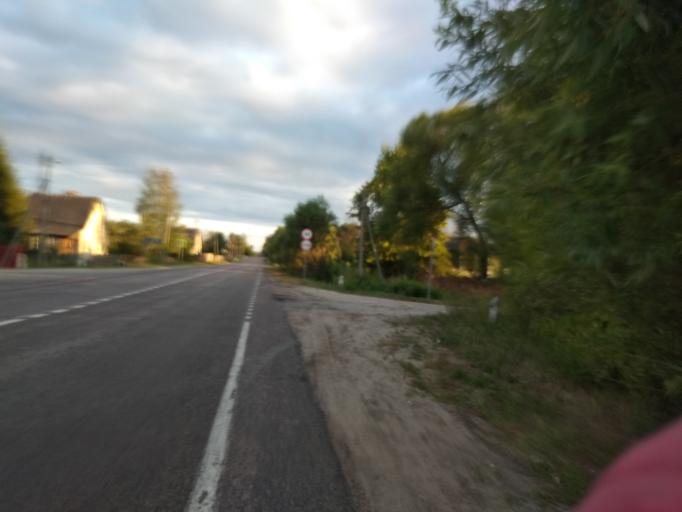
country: RU
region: Moskovskaya
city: Misheronskiy
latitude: 55.6028
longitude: 39.7072
